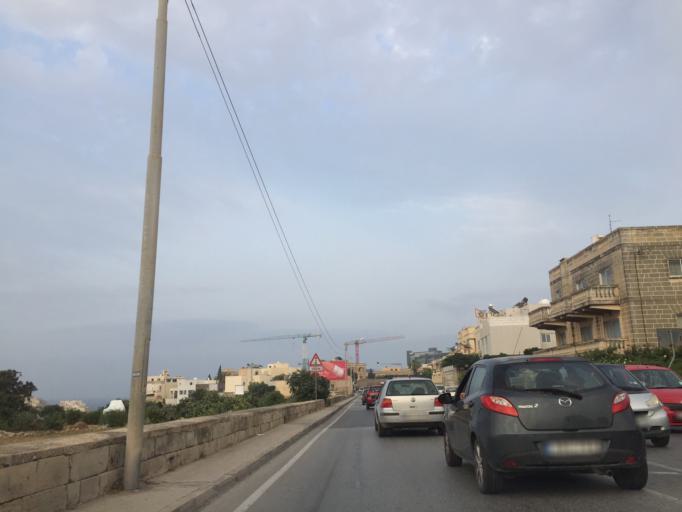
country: MT
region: Is-Swieqi
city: Swieqi
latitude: 35.9234
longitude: 14.4821
